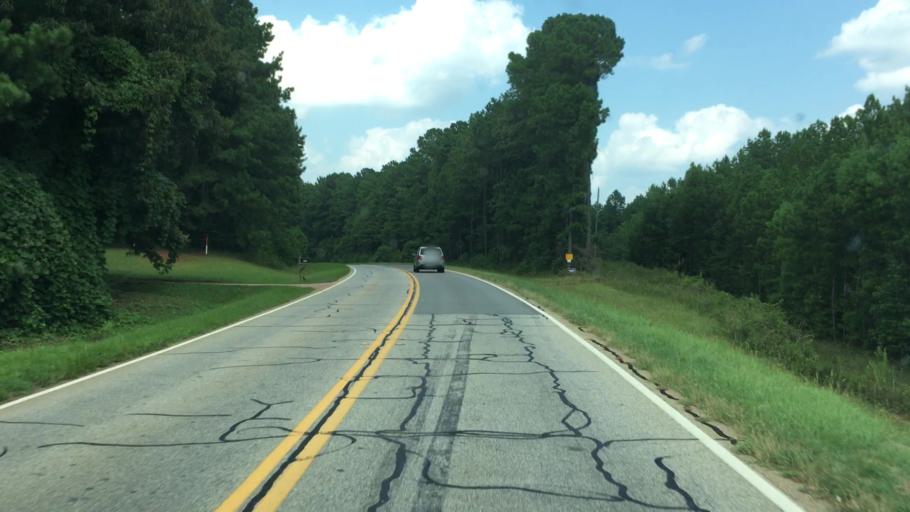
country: US
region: Georgia
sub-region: Jasper County
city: Monticello
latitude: 33.2405
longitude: -83.7240
